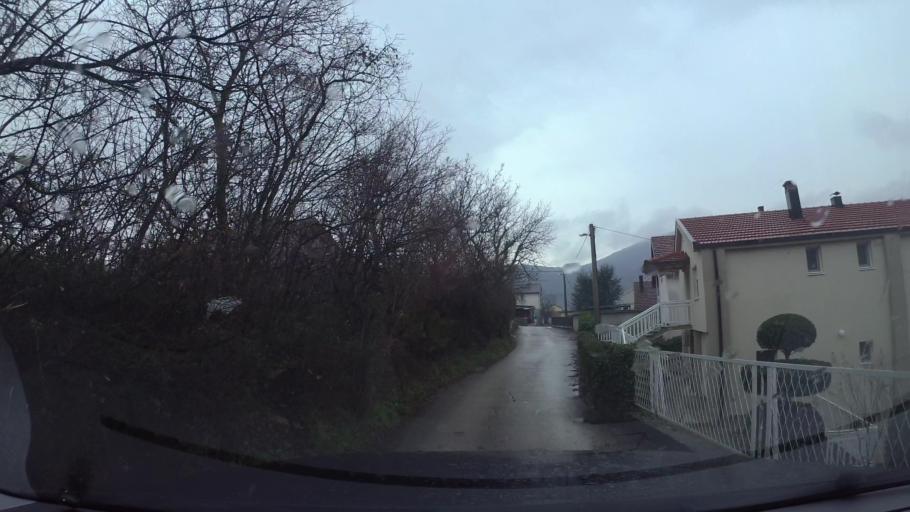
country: BA
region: Federation of Bosnia and Herzegovina
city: Cim
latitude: 43.3503
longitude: 17.7805
